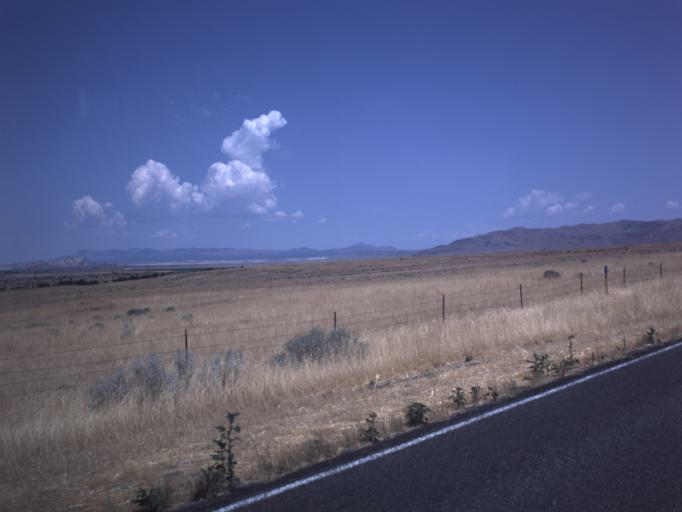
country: US
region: Utah
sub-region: Millard County
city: Delta
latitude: 39.4442
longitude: -112.3124
